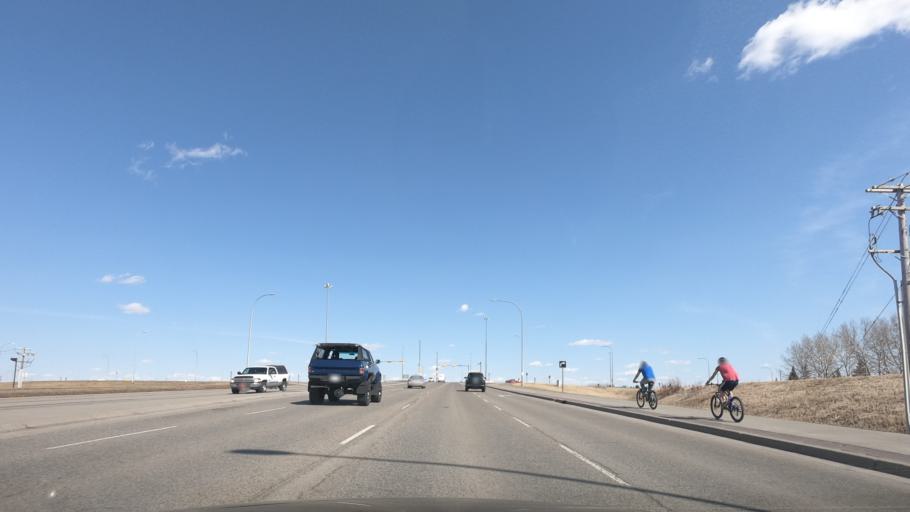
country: CA
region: Alberta
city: Airdrie
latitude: 51.3000
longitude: -114.0059
